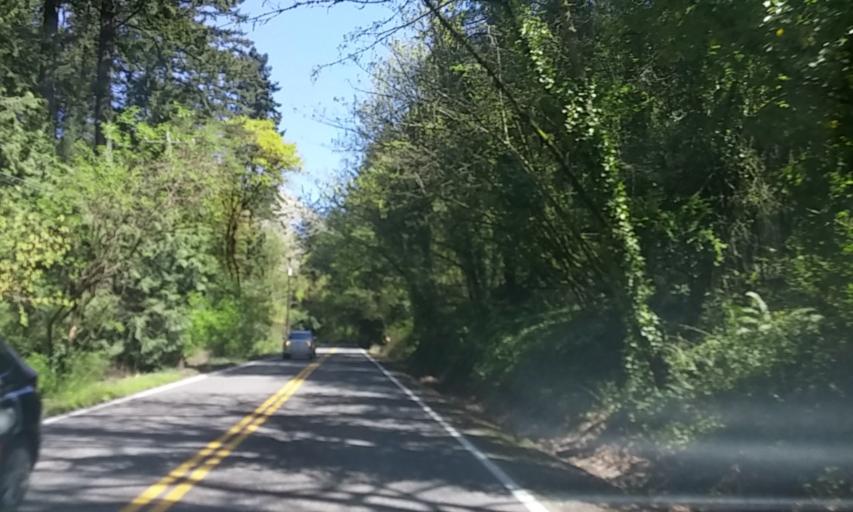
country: US
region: Oregon
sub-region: Washington County
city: West Haven
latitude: 45.5301
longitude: -122.7598
